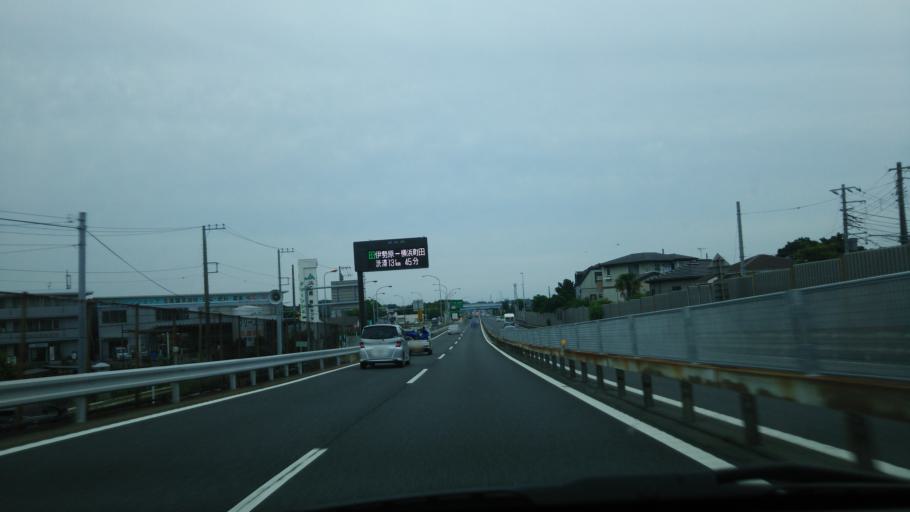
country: JP
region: Kanagawa
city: Isehara
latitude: 35.3592
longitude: 139.3030
